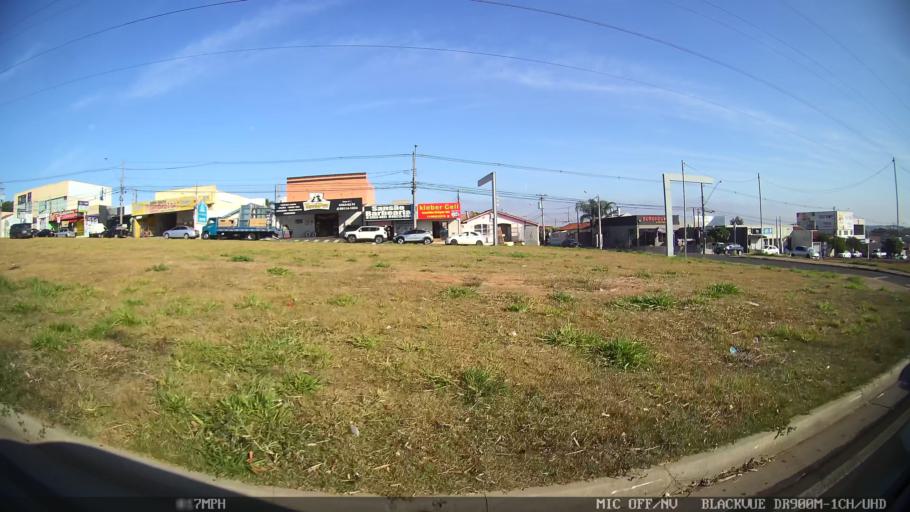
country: BR
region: Sao Paulo
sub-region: Sao Jose Do Rio Preto
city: Sao Jose do Rio Preto
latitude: -20.7890
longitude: -49.3439
